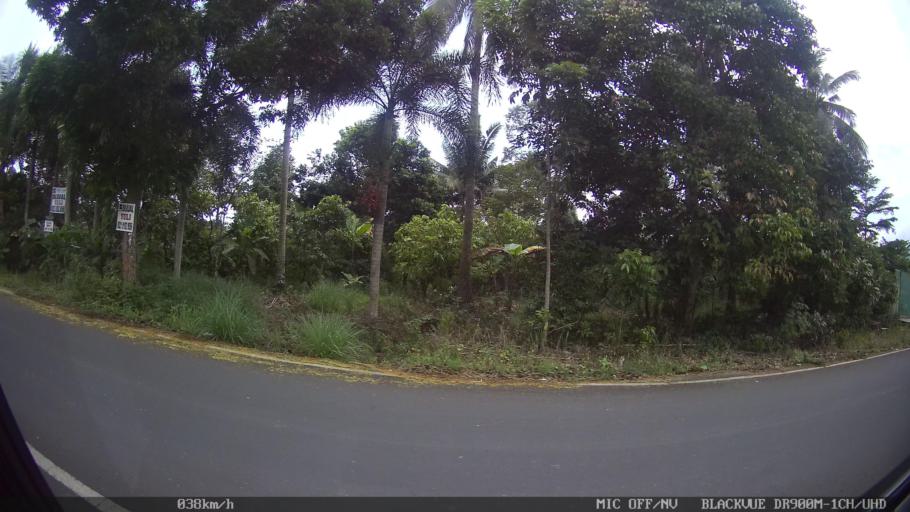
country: ID
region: Lampung
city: Bandarlampung
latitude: -5.4302
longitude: 105.2081
